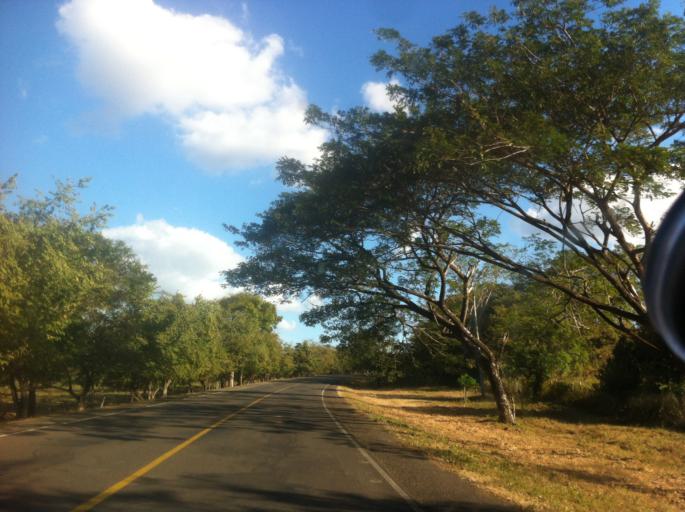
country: NI
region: Chontales
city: Acoyapa
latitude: 11.8794
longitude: -85.0920
